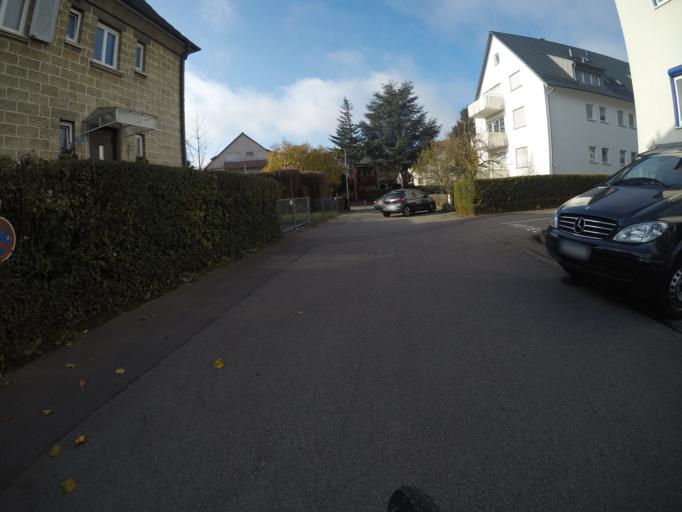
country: DE
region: Baden-Wuerttemberg
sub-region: Regierungsbezirk Stuttgart
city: Leinfelden-Echterdingen
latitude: 48.7210
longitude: 9.1446
